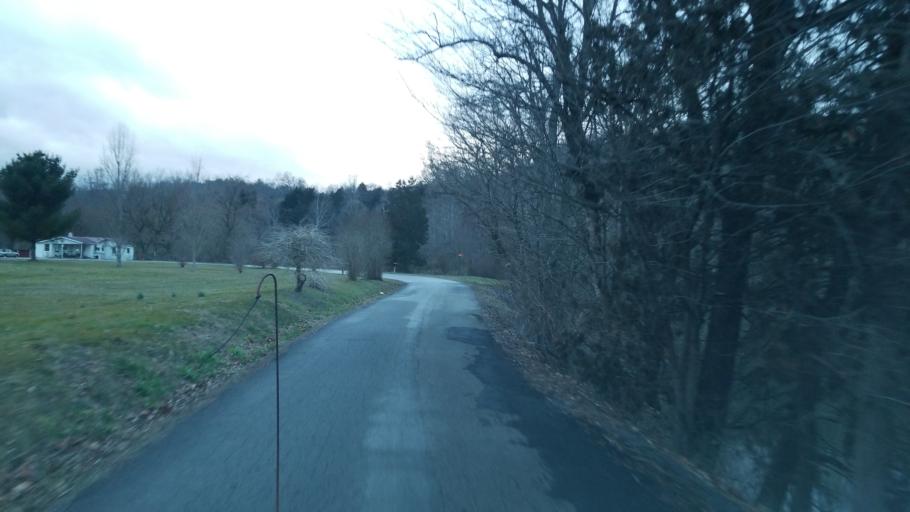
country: US
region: Virginia
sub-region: Pulaski County
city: Pulaski
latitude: 37.1607
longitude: -80.8665
